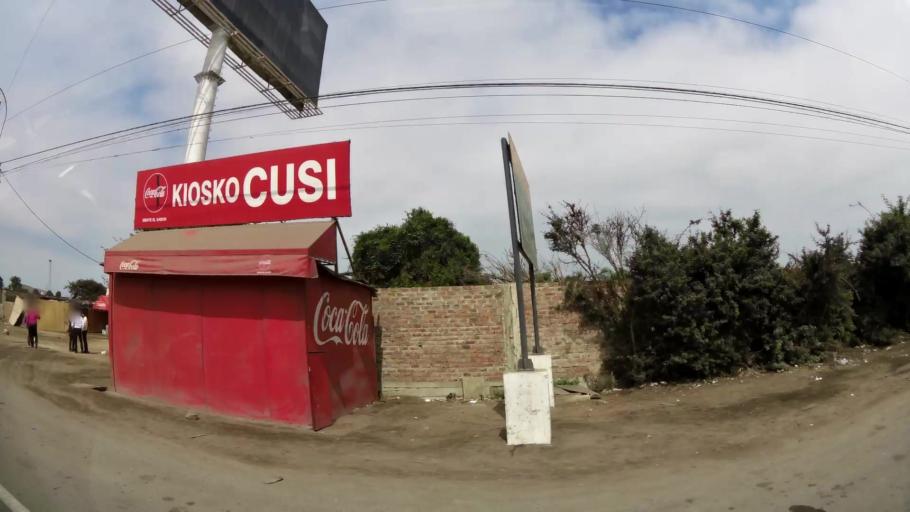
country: PE
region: Lima
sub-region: Provincia de Canete
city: Mala
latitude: -12.7135
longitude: -76.6288
